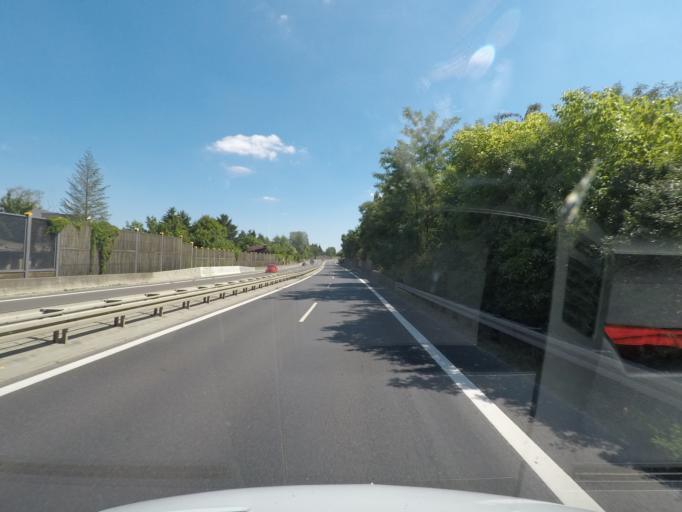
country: DE
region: Berlin
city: Bohnsdorf
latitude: 52.3962
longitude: 13.5608
